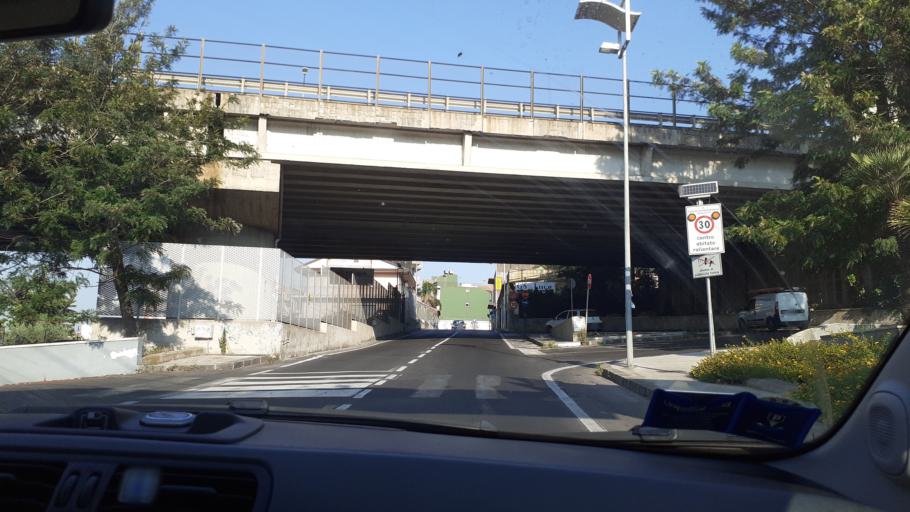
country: IT
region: Sicily
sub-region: Catania
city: Misterbianco
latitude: 37.5159
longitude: 15.0204
